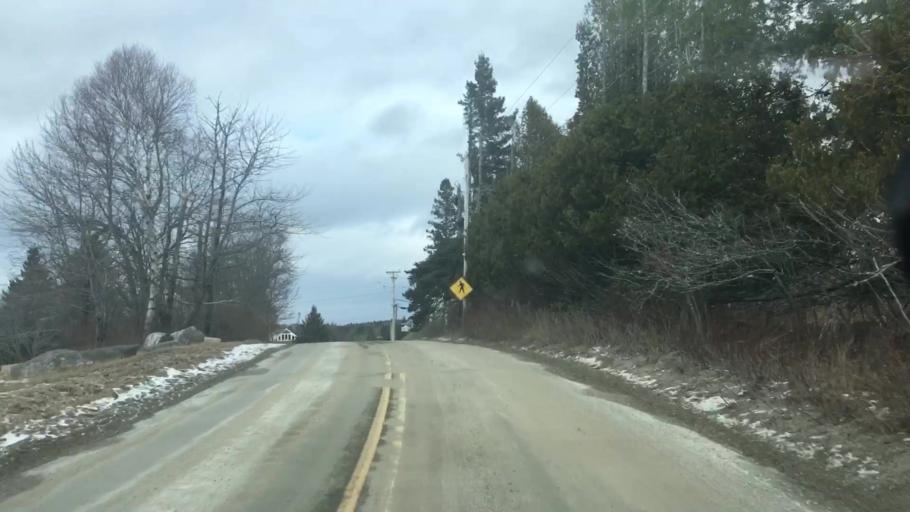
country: US
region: Maine
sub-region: Washington County
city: Machias
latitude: 44.6122
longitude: -67.4804
